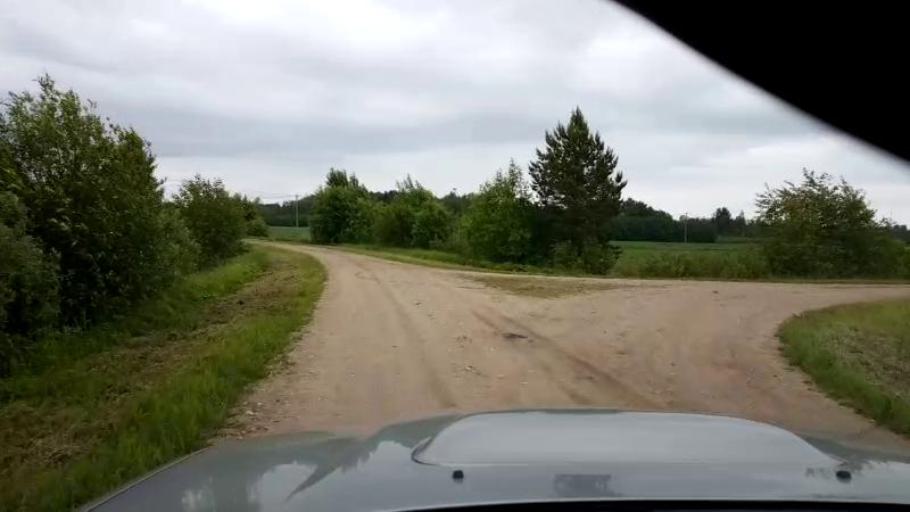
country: EE
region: Paernumaa
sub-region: Halinga vald
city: Parnu-Jaagupi
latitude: 58.5618
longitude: 24.5767
